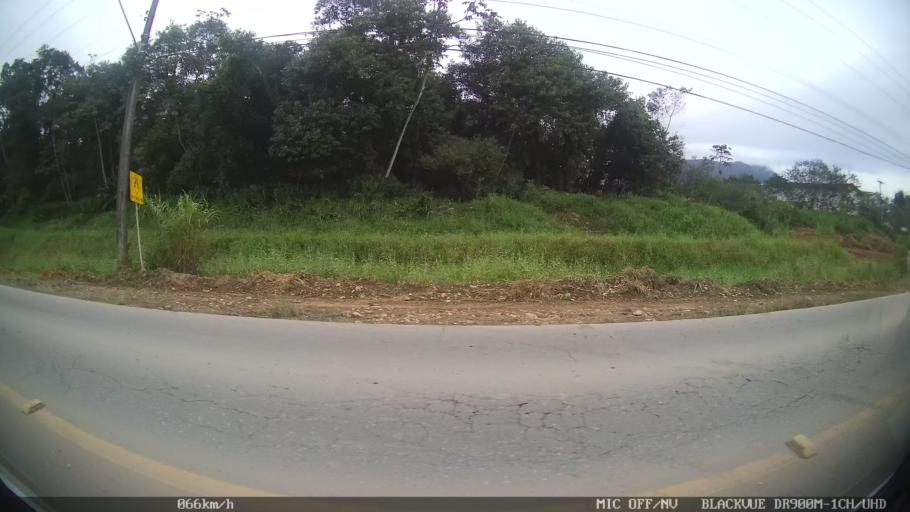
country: BR
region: Santa Catarina
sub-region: Joinville
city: Joinville
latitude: -26.2360
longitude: -48.8947
